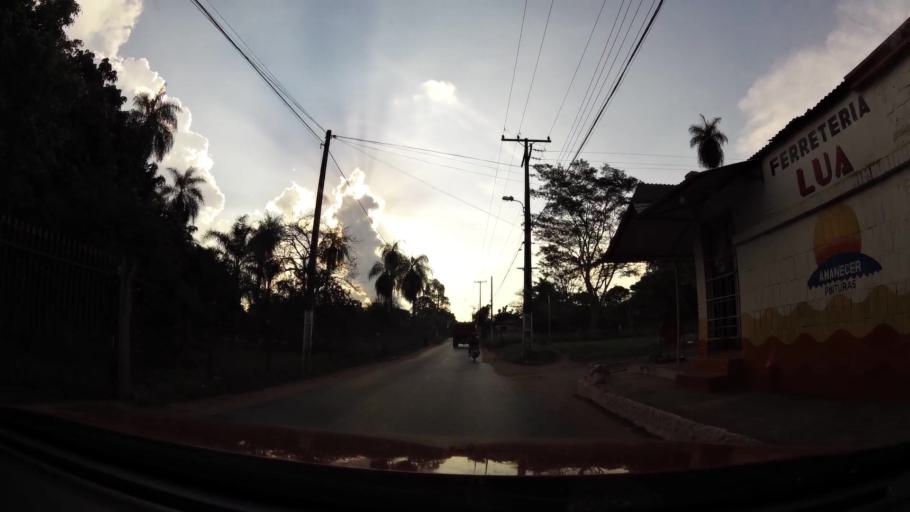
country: PY
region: Central
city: Nemby
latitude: -25.3694
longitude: -57.5296
